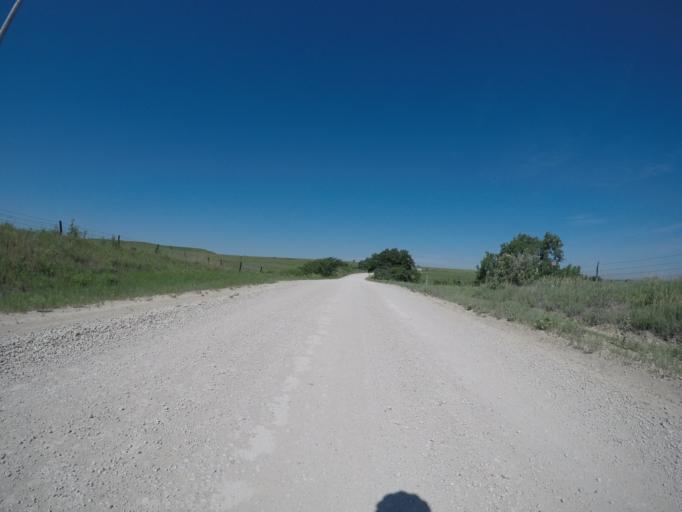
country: US
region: Kansas
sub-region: Wabaunsee County
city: Alma
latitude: 39.0152
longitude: -96.1389
